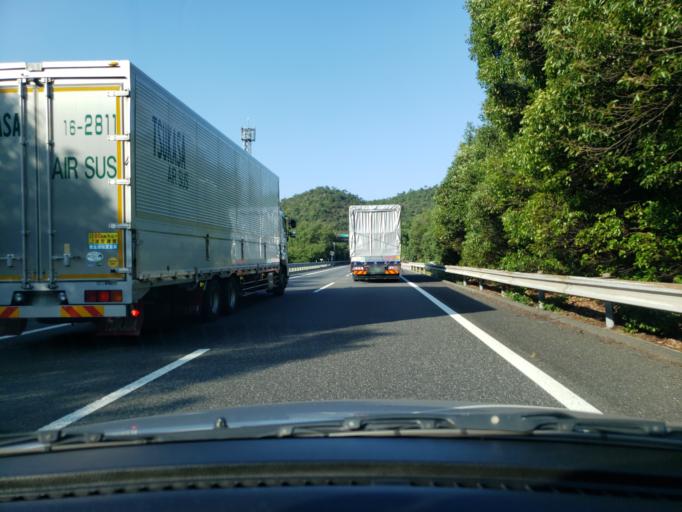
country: JP
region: Okayama
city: Kurashiki
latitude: 34.6158
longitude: 133.7393
